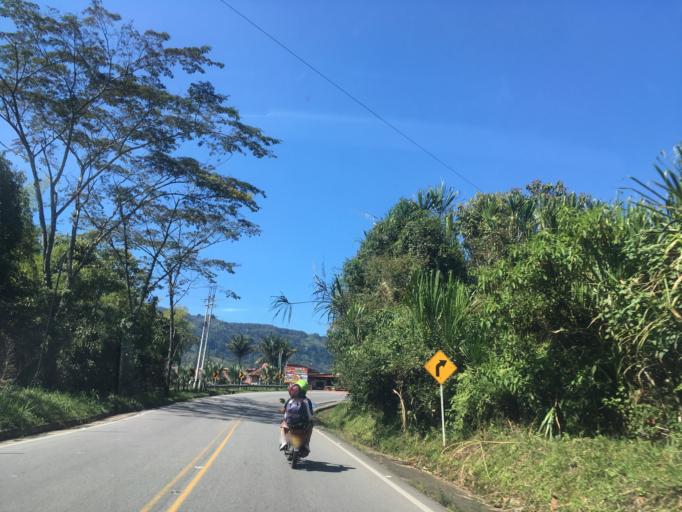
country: CO
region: Santander
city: Suaita
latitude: 6.0859
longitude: -73.3865
